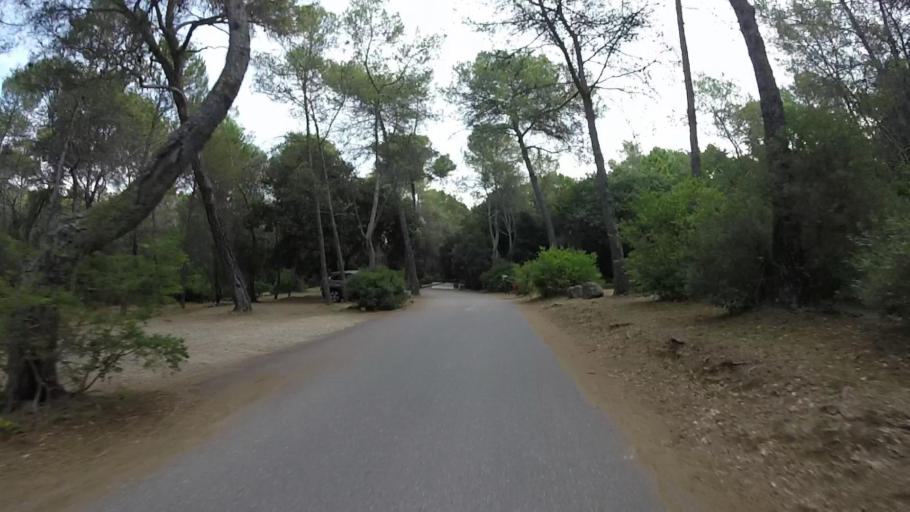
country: FR
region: Provence-Alpes-Cote d'Azur
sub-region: Departement des Alpes-Maritimes
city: Vallauris
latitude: 43.6066
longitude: 7.0412
